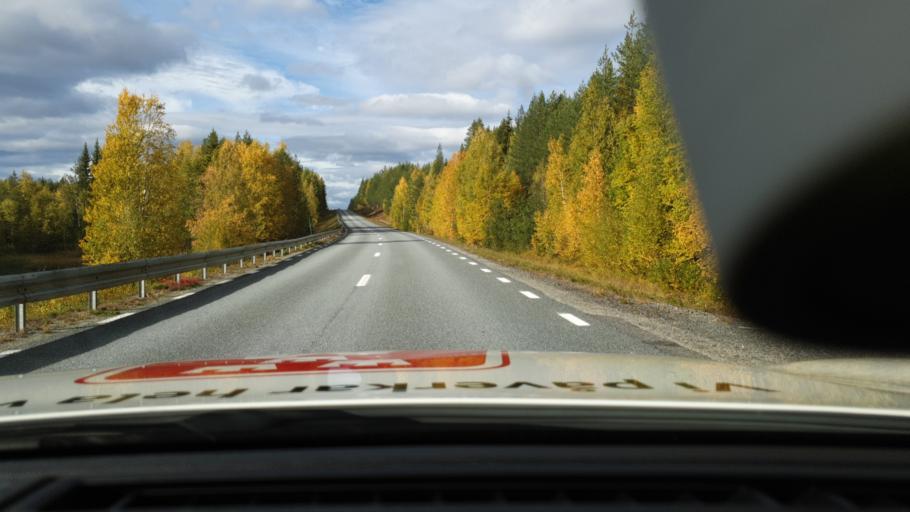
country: SE
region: Vaesterbotten
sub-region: Mala Kommun
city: Mala
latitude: 65.0268
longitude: 18.4293
